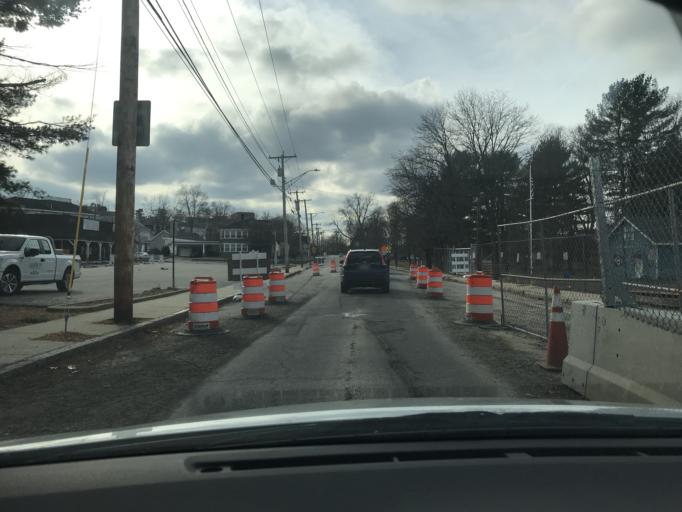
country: US
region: Massachusetts
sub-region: Middlesex County
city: Lowell
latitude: 42.6467
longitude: -71.3321
